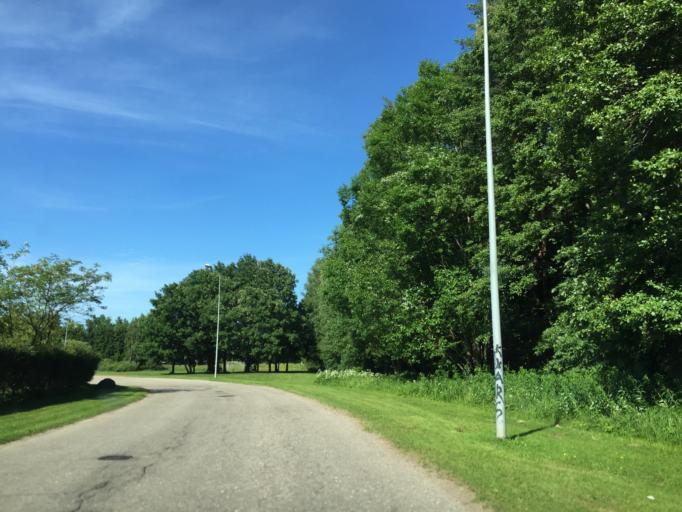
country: LV
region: Babite
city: Pinki
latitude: 56.9549
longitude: 23.9554
